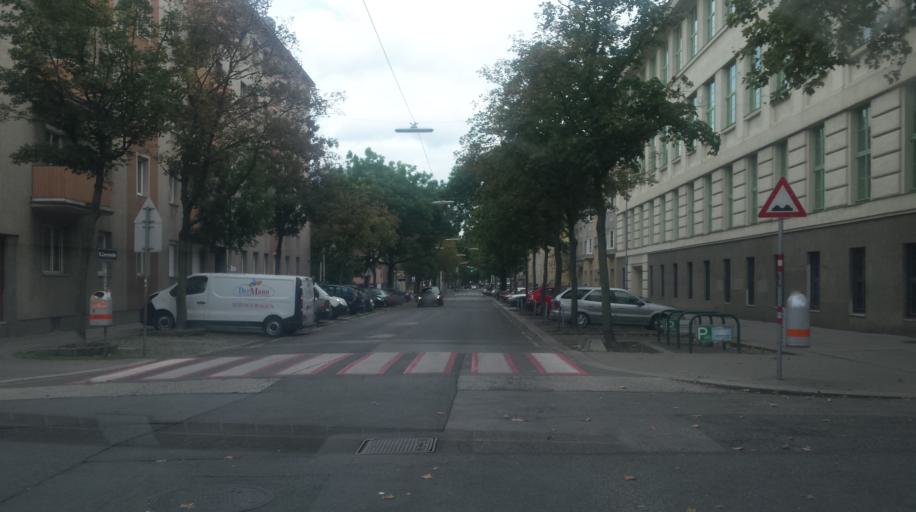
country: AT
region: Vienna
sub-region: Wien Stadt
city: Vienna
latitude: 48.1737
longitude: 16.4120
